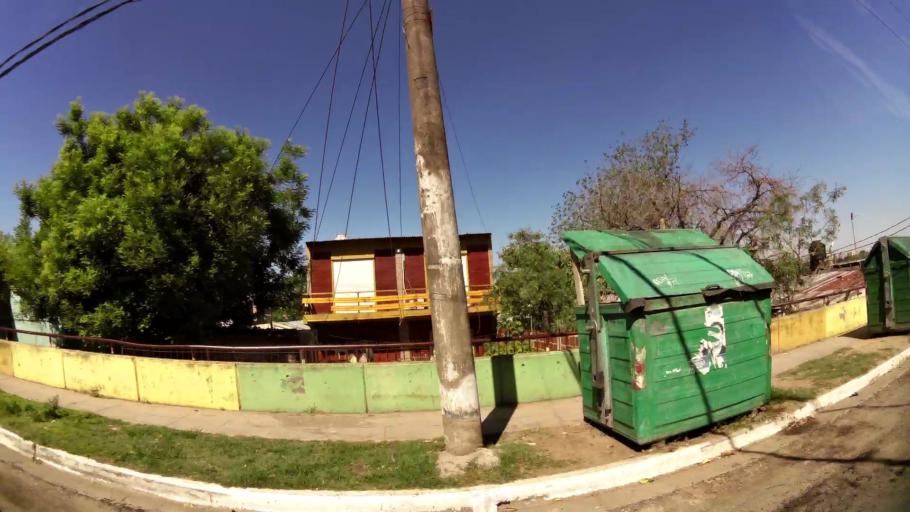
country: AR
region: Buenos Aires
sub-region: Partido de Quilmes
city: Quilmes
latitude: -34.7059
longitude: -58.2999
